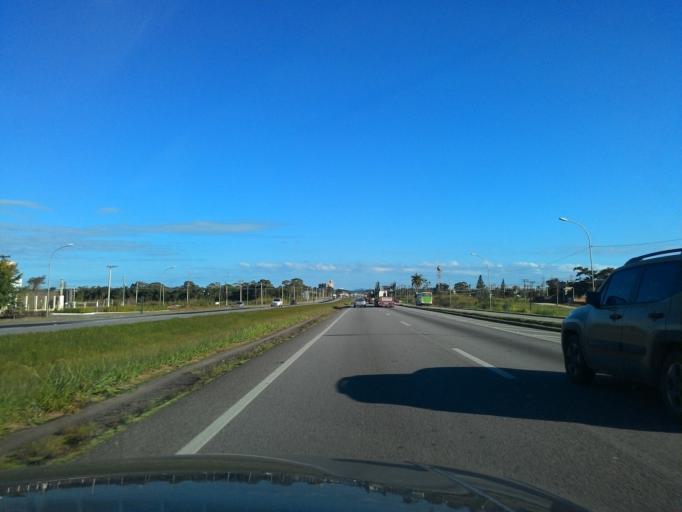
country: BR
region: Sao Paulo
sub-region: Registro
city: Registro
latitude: -24.5166
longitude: -47.8522
